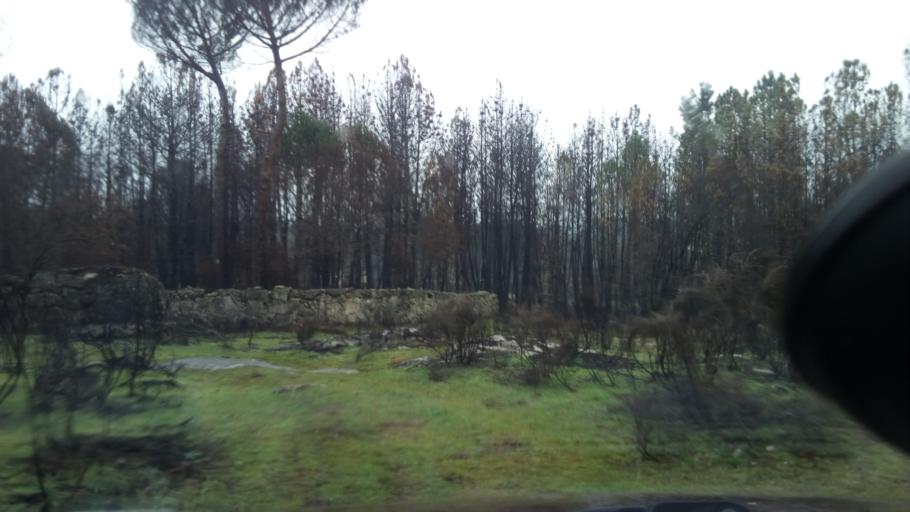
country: PT
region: Viseu
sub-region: Mangualde
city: Mangualde
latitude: 40.6147
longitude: -7.7848
